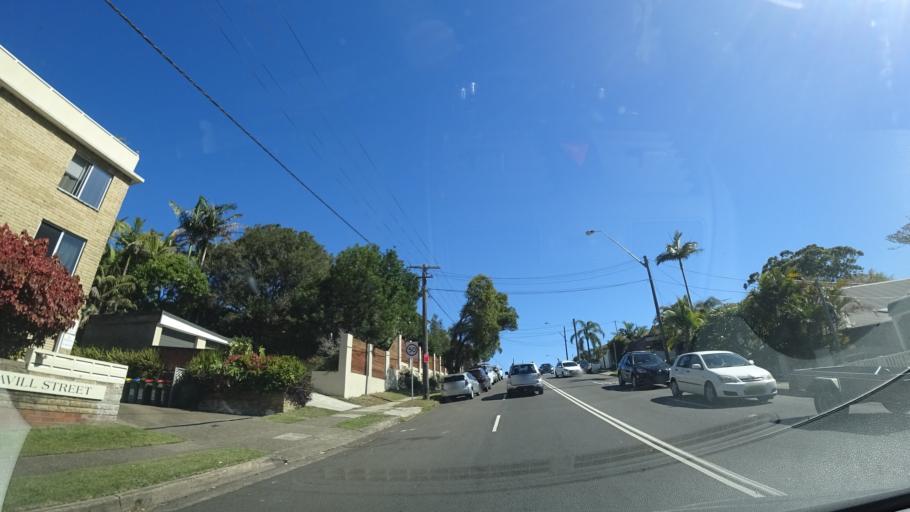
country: AU
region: New South Wales
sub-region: Warringah
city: Freshwater
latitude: -33.7800
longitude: 151.2822
